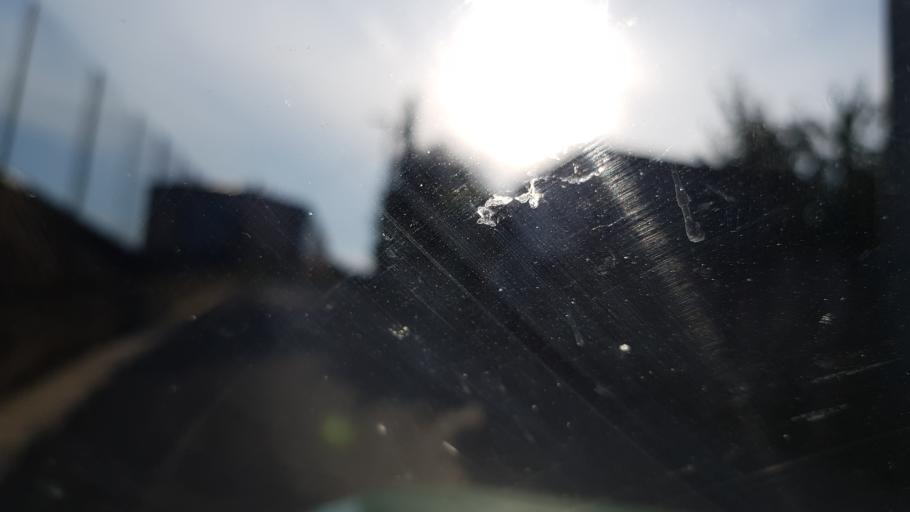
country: IT
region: Friuli Venezia Giulia
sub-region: Provincia di Trieste
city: Trieste
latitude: 45.6167
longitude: 13.7948
